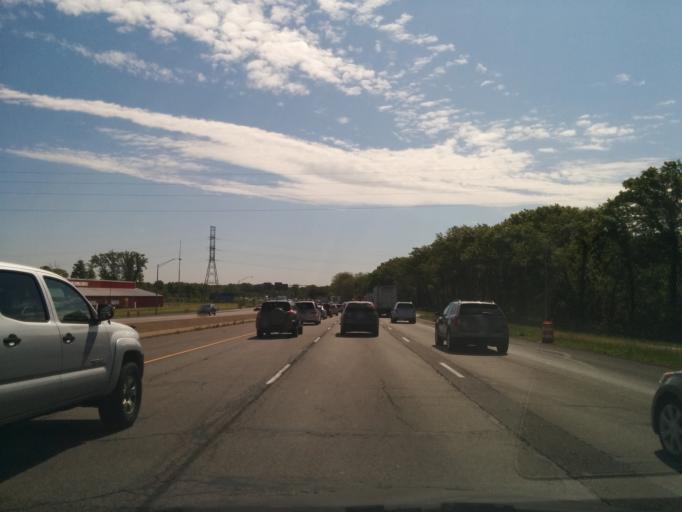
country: US
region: Indiana
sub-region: Porter County
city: Porter
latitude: 41.6071
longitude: -87.1055
